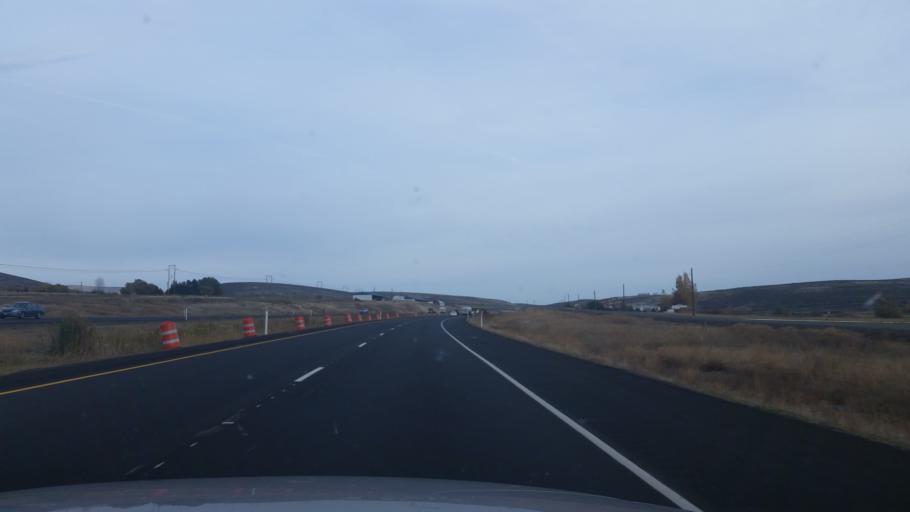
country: US
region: Washington
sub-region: Kittitas County
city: Kittitas
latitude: 46.9728
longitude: -120.3776
